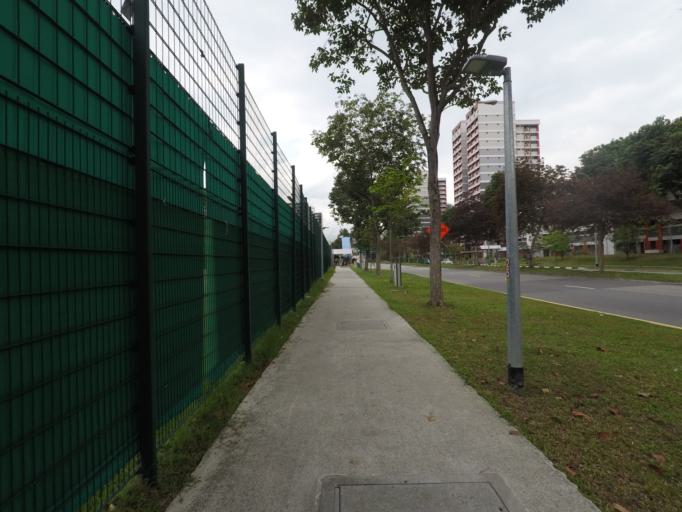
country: MY
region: Johor
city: Kampung Pasir Gudang Baru
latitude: 1.3774
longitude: 103.8927
